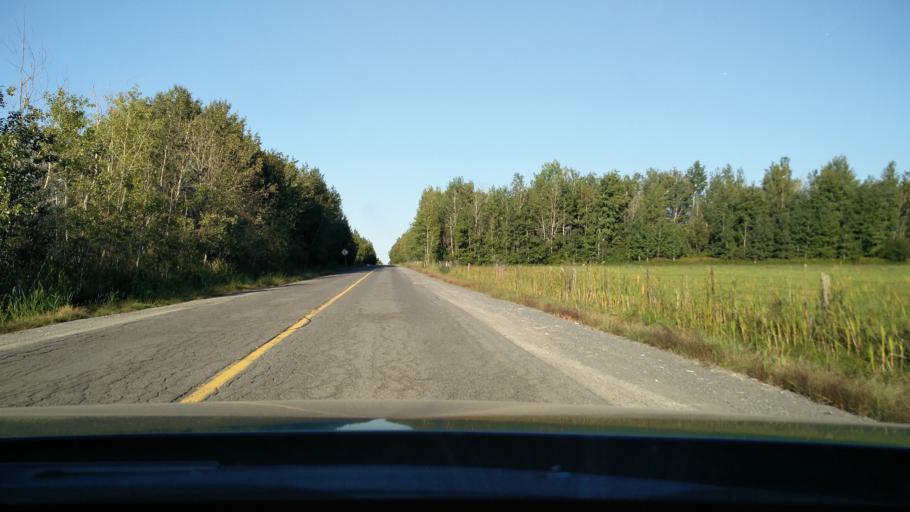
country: CA
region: Ontario
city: Bells Corners
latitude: 45.2174
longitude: -75.7713
